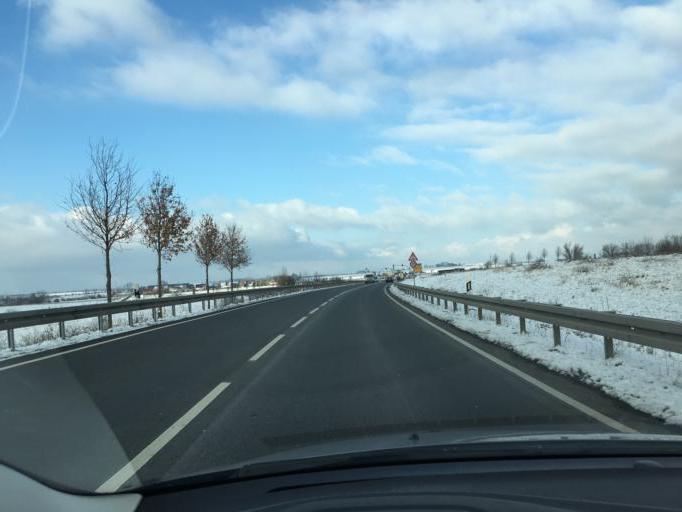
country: DE
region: Saxony
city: Grimma
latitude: 51.2293
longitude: 12.6971
